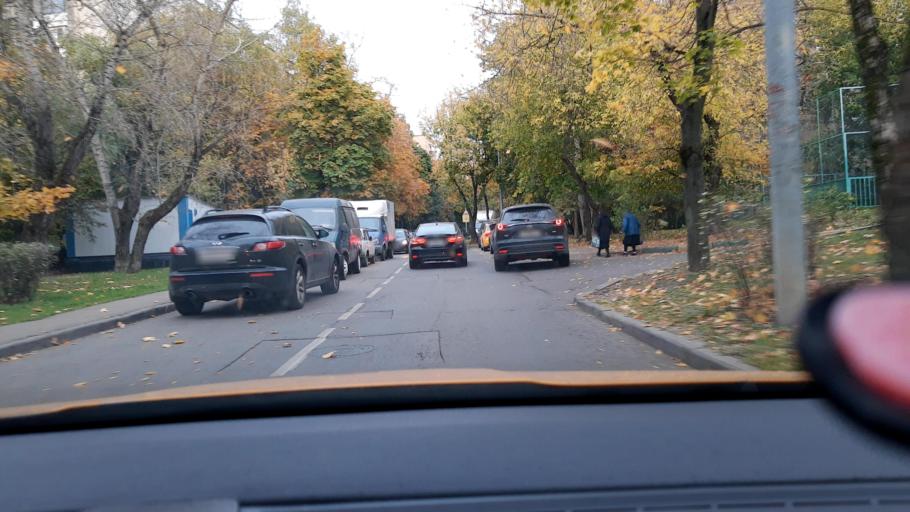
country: RU
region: Moskovskaya
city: Bol'shaya Setun'
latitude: 55.7251
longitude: 37.4370
